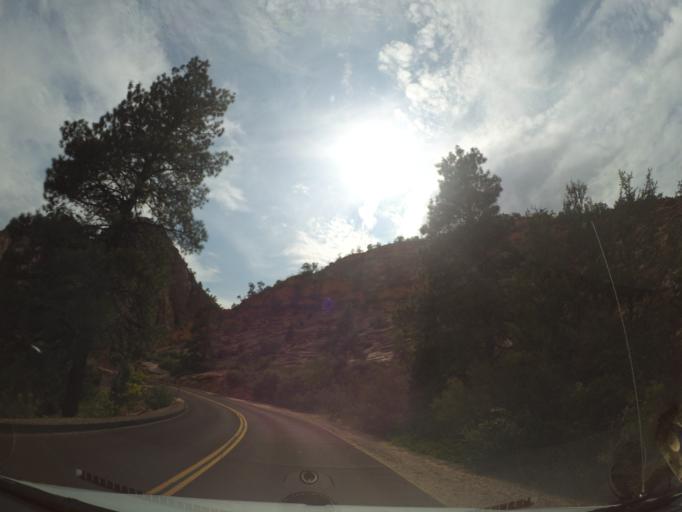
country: US
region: Utah
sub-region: Washington County
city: Hildale
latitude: 37.2156
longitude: -112.9311
